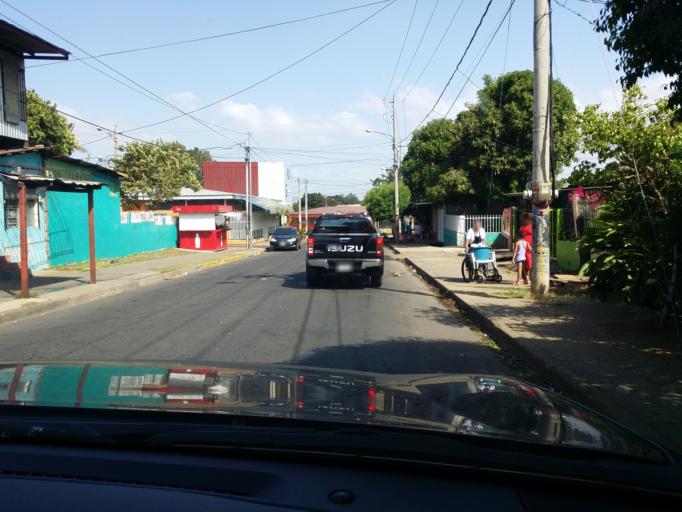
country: NI
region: Managua
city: Managua
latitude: 12.1294
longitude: -86.2301
